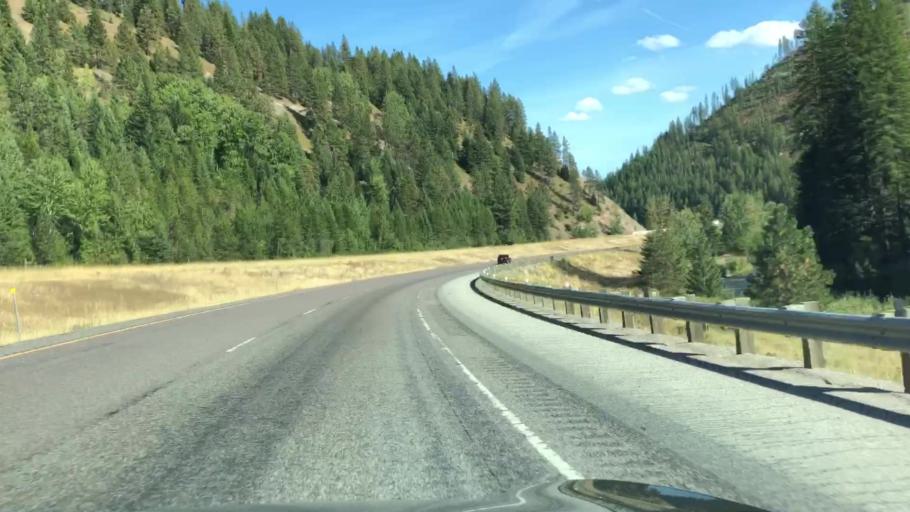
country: US
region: Montana
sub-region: Sanders County
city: Thompson Falls
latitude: 47.4039
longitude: -115.4775
